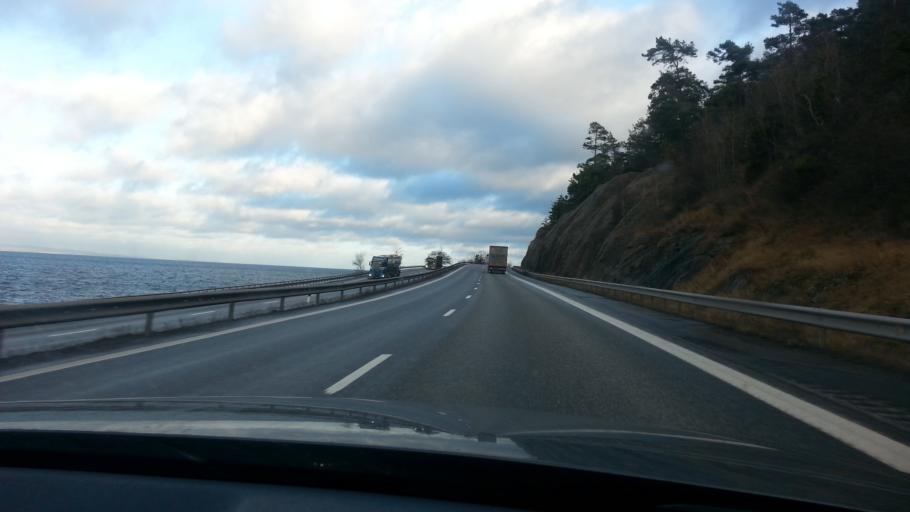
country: SE
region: Joenkoeping
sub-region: Jonkopings Kommun
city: Kaxholmen
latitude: 57.8673
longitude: 14.2708
